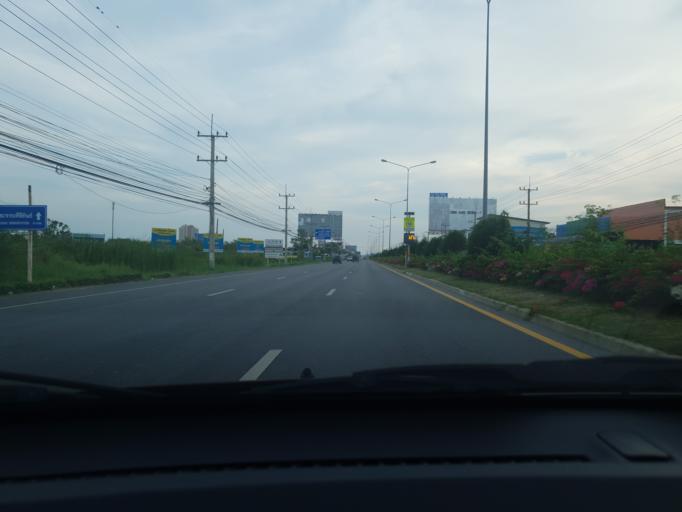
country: TH
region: Phetchaburi
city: Cha-am
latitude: 12.7757
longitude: 99.9669
